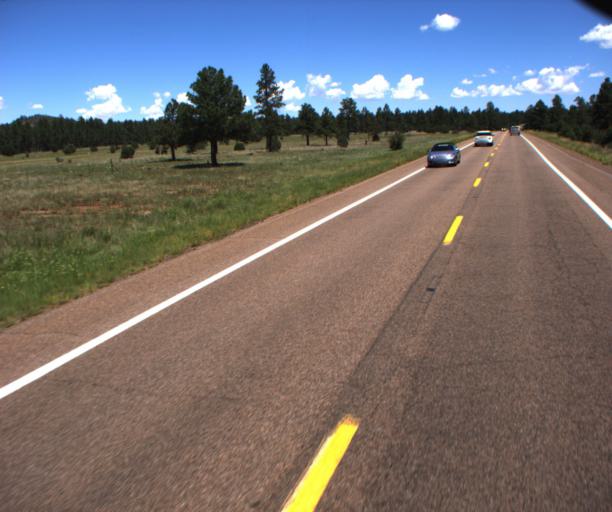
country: US
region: Arizona
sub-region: Navajo County
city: Lake of the Woods
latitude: 34.1089
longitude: -110.1501
